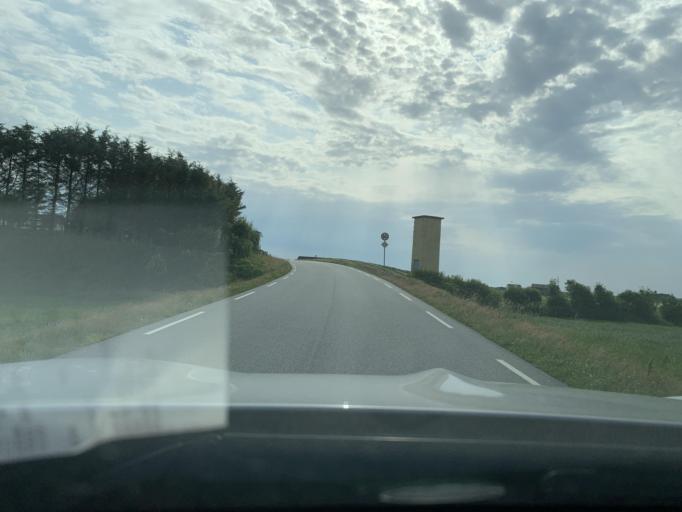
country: NO
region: Rogaland
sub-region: Time
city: Bryne
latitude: 58.7240
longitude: 5.5795
